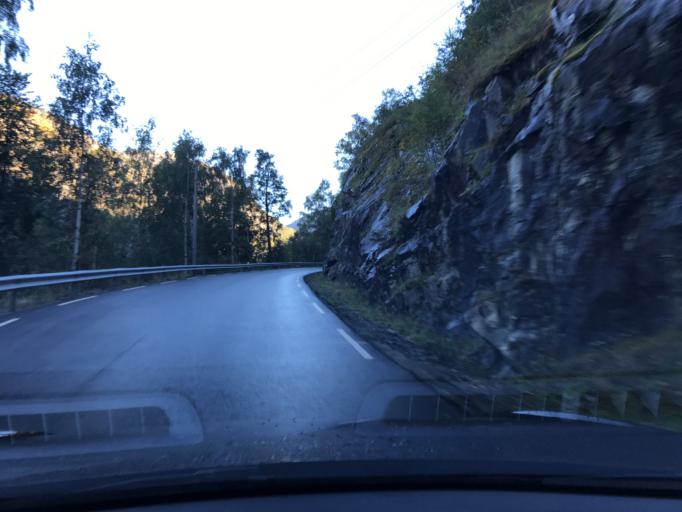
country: NO
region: Sogn og Fjordane
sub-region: Aurland
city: Aurlandsvangen
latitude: 60.8610
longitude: 7.3045
